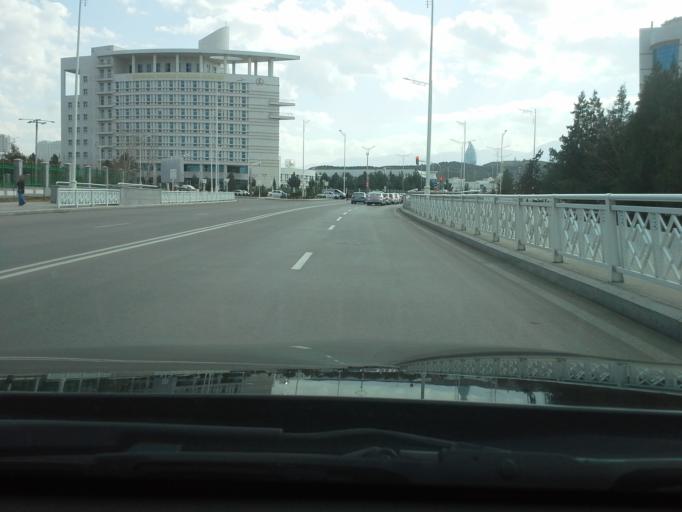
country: TM
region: Ahal
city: Ashgabat
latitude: 37.9533
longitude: 58.3393
